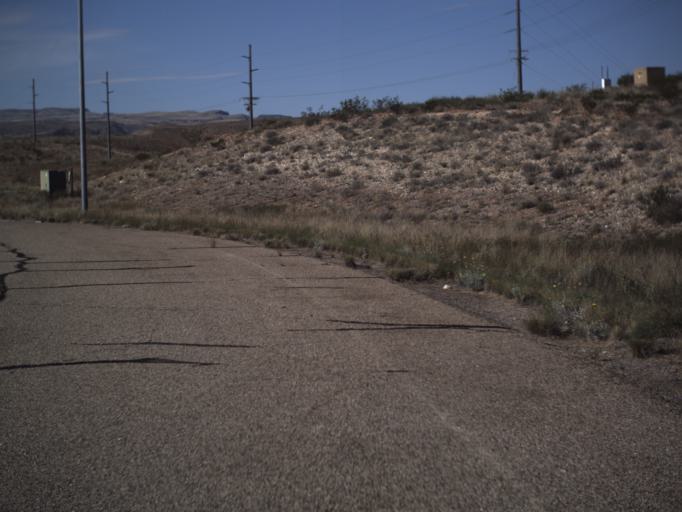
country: US
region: Utah
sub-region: Washington County
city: Saint George
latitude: 37.0162
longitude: -113.6137
